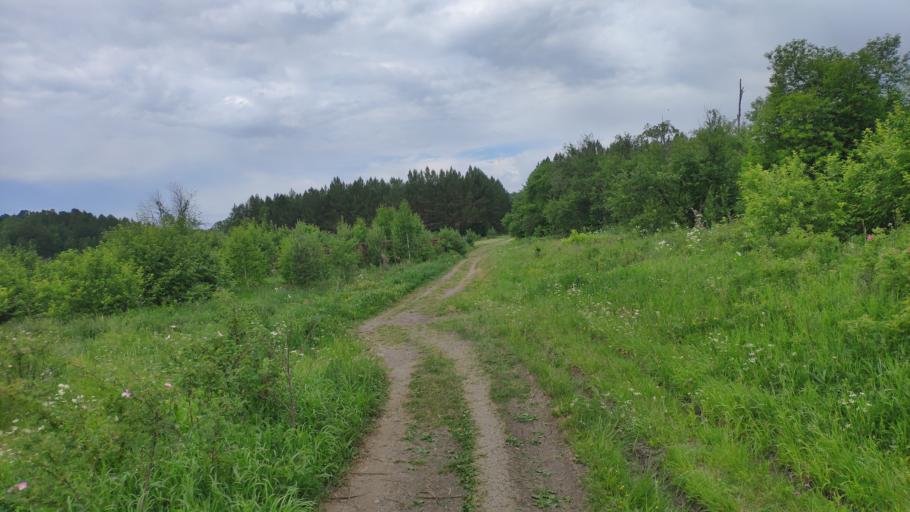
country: RU
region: Bashkortostan
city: Abzakovo
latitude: 53.8165
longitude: 58.6357
